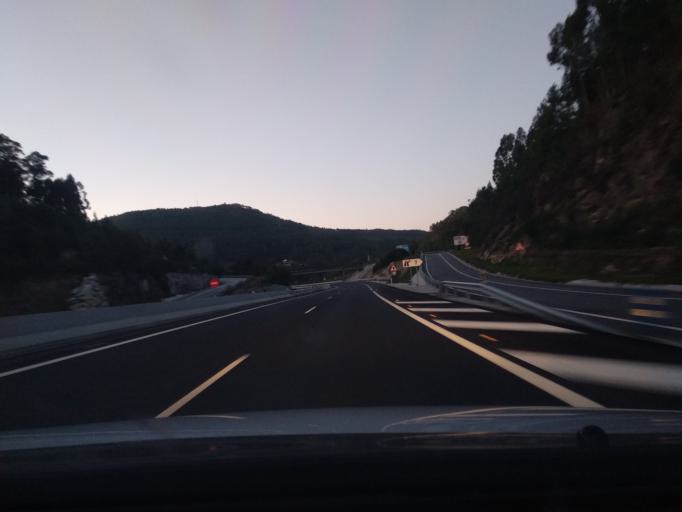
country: ES
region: Galicia
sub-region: Provincia de Pontevedra
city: Moana
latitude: 42.3025
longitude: -8.7202
